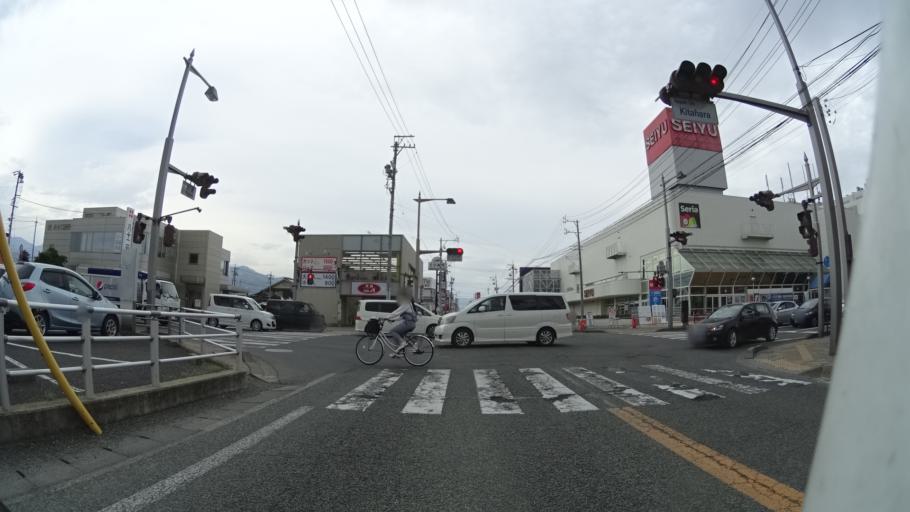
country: JP
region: Nagano
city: Nagano-shi
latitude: 36.5939
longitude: 138.1561
